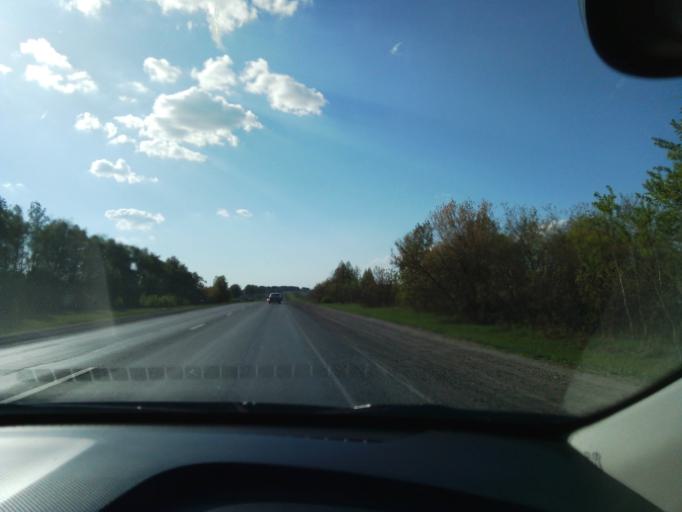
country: RU
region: Chuvashia
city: Kugesi
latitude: 56.0584
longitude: 47.2604
